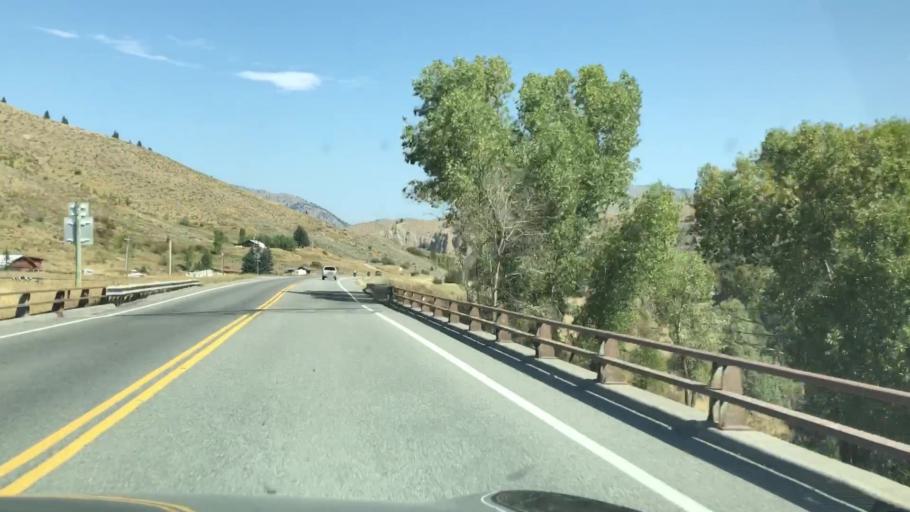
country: US
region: Wyoming
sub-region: Teton County
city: Hoback
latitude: 43.3447
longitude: -110.7222
